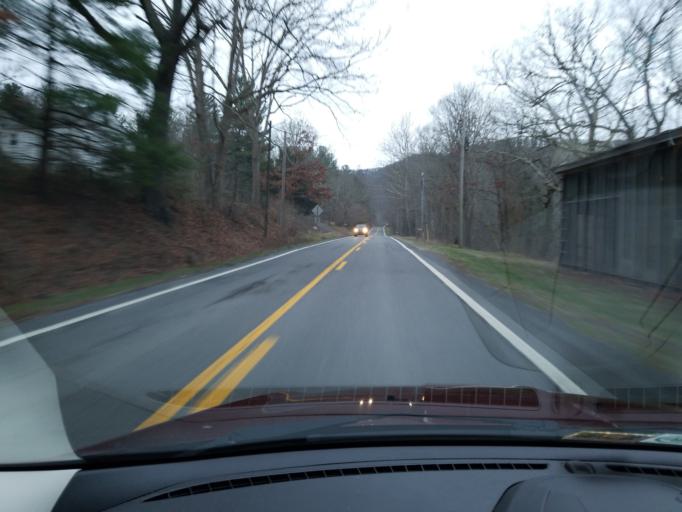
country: US
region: West Virginia
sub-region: Monroe County
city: Union
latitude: 37.5237
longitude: -80.6172
